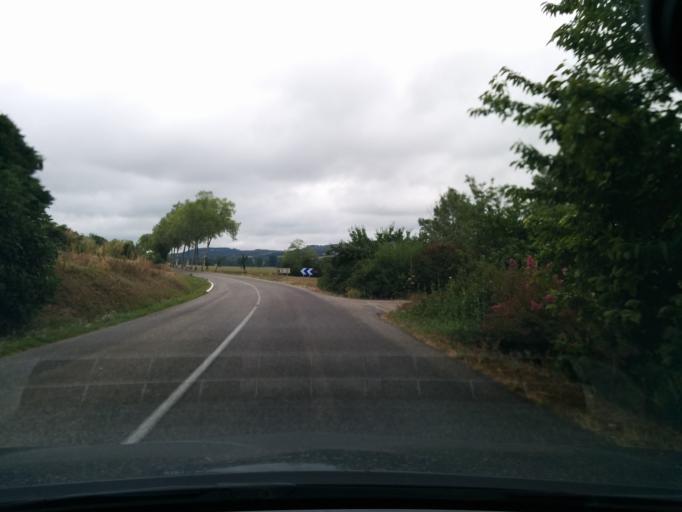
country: FR
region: Midi-Pyrenees
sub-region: Departement du Tarn-et-Garonne
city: Lauzerte
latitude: 44.2349
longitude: 1.0886
